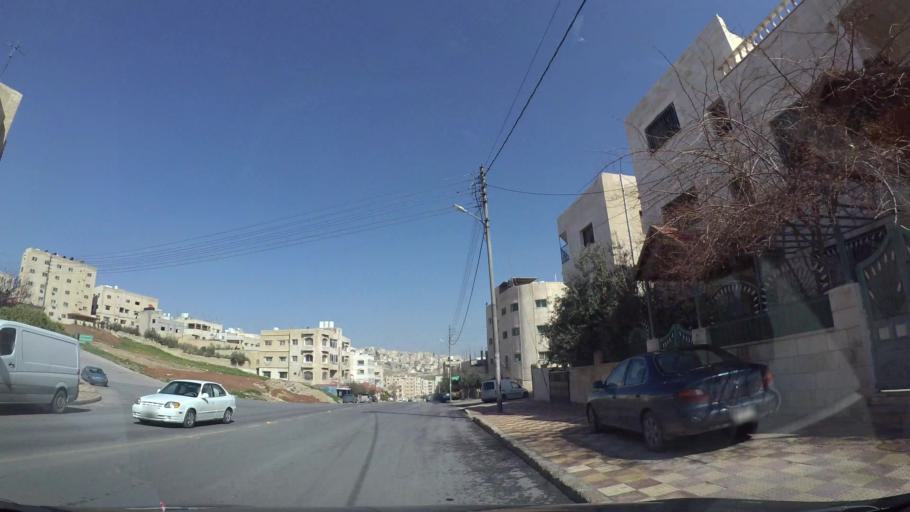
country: JO
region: Amman
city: Amman
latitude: 31.9869
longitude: 35.9835
